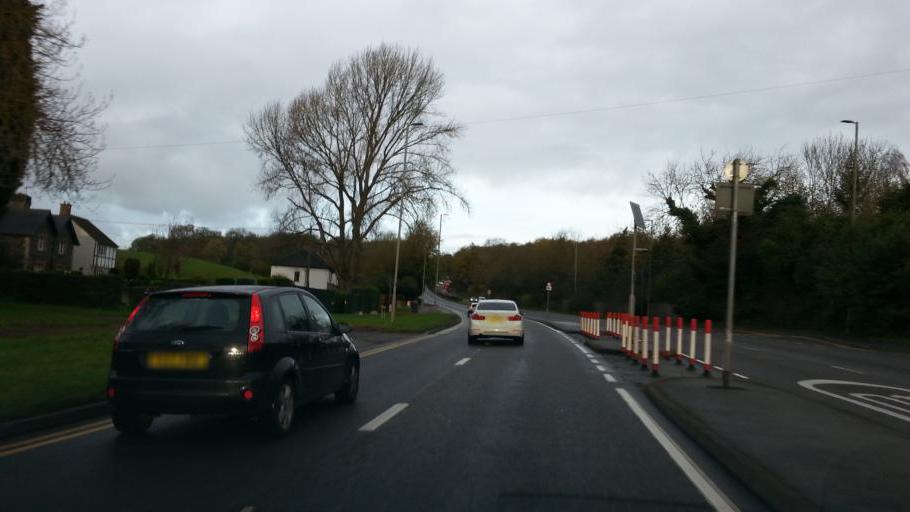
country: GB
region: England
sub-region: Leicestershire
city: Markfield
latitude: 52.6702
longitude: -1.2445
